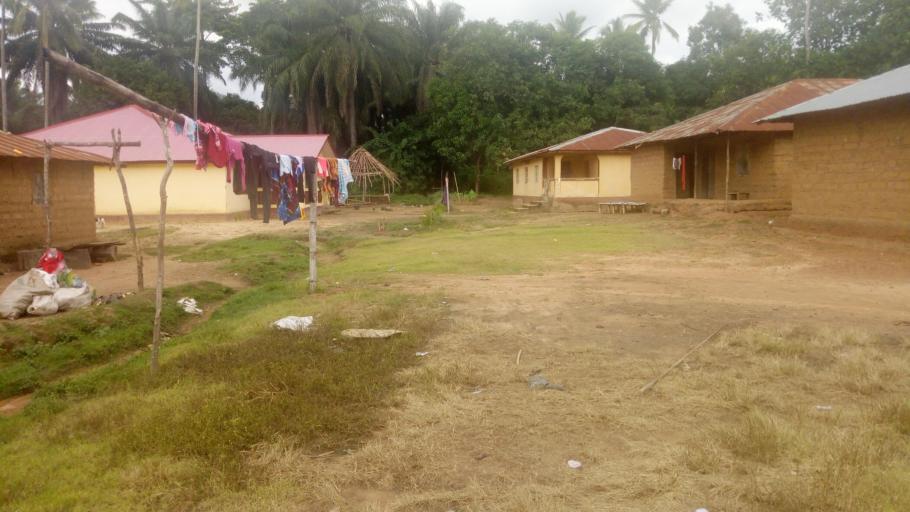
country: SL
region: Northern Province
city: Magburaka
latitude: 8.6796
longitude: -12.0304
